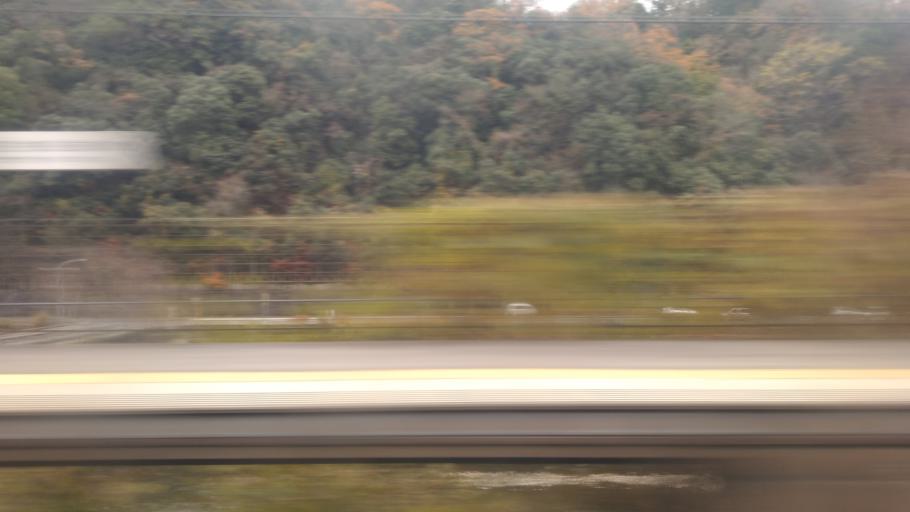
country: JP
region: Gifu
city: Tajimi
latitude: 35.3031
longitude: 137.1011
